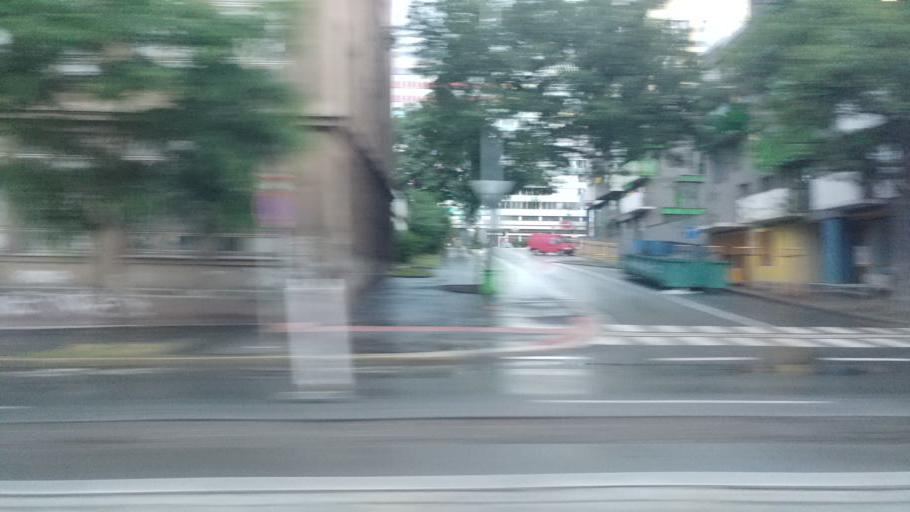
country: CZ
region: Praha
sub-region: Praha 8
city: Karlin
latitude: 50.0680
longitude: 14.4637
